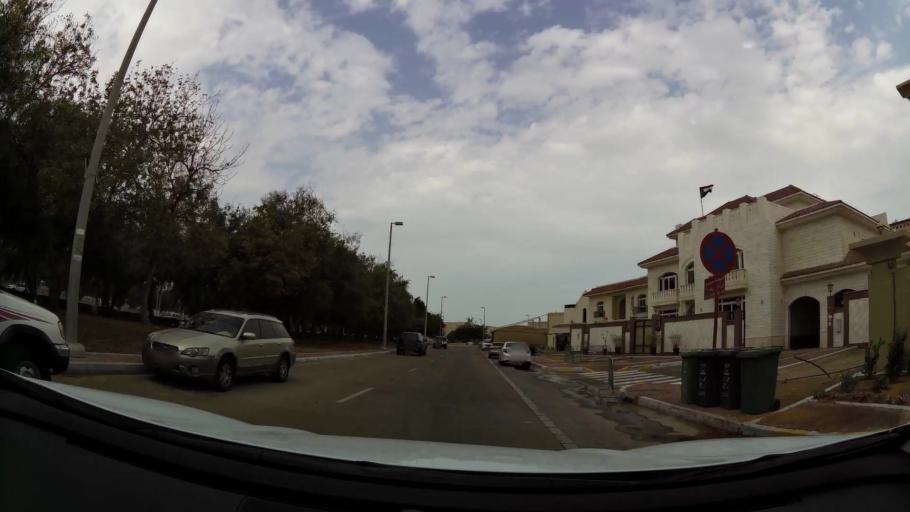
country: AE
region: Abu Dhabi
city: Abu Dhabi
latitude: 24.4308
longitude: 54.4424
